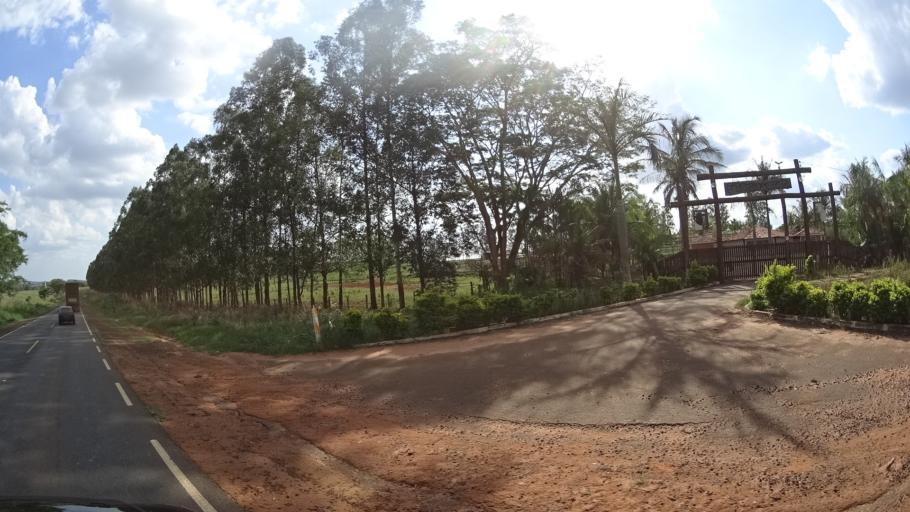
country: BR
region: Sao Paulo
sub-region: Urupes
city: Urupes
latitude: -21.1754
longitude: -49.2912
